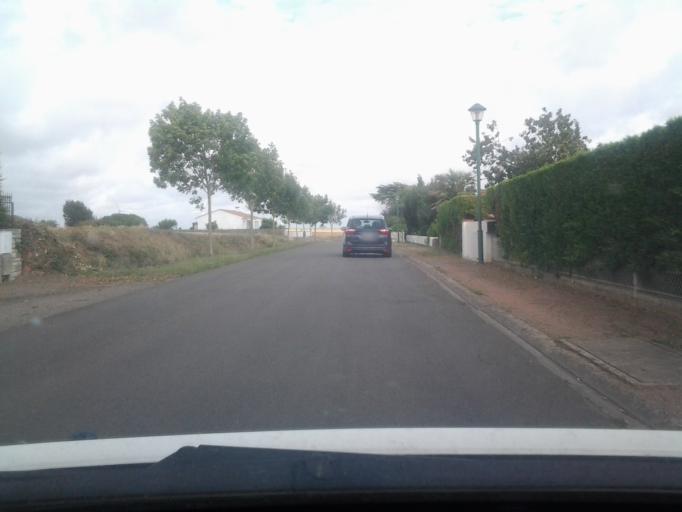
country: FR
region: Pays de la Loire
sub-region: Departement de la Vendee
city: Longeville-sur-Mer
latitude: 46.4225
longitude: -1.4832
